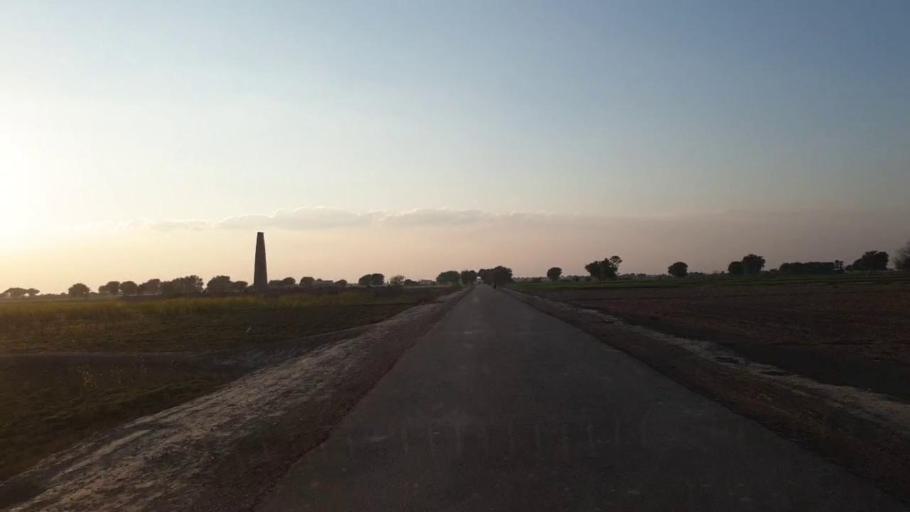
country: PK
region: Sindh
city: Shahpur Chakar
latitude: 26.1558
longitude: 68.5574
